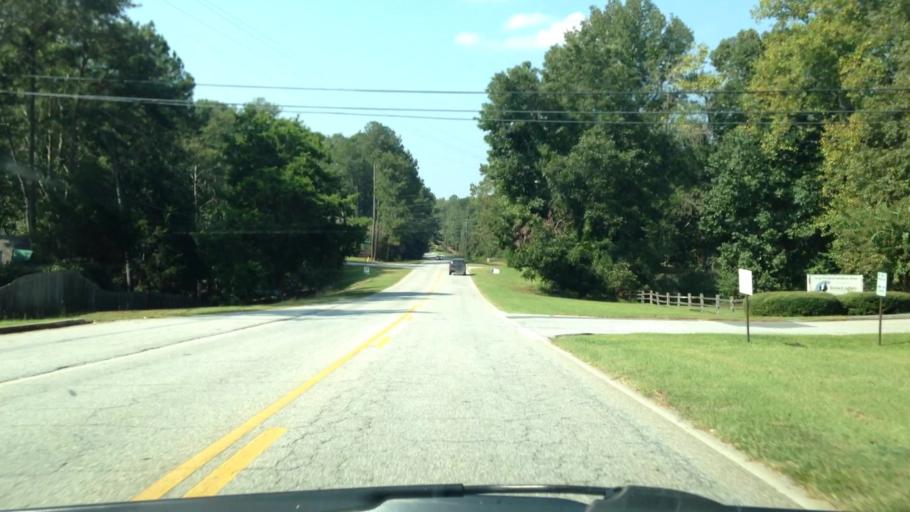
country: US
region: Alabama
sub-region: Russell County
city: Phenix City
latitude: 32.5559
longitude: -84.9851
